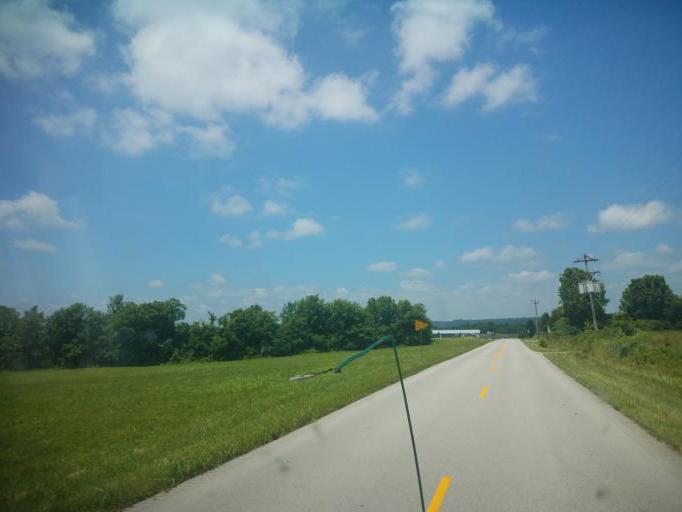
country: US
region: Kentucky
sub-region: Edmonson County
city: Brownsville
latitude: 37.3238
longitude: -86.1183
